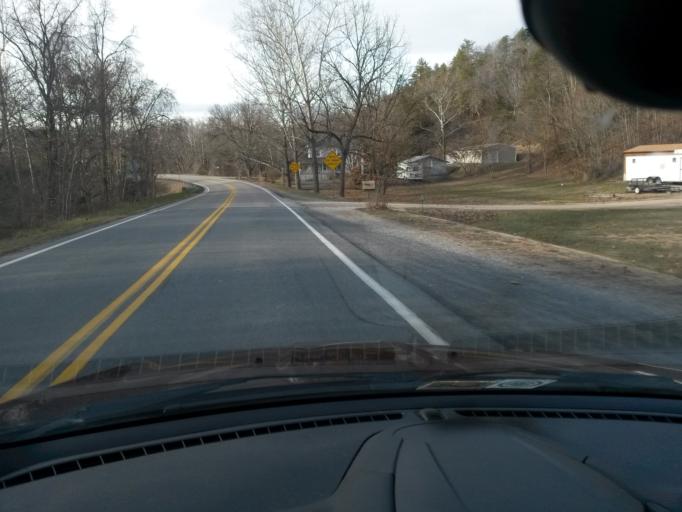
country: US
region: Virginia
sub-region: Bath County
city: Warm Springs
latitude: 37.9954
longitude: -79.6203
